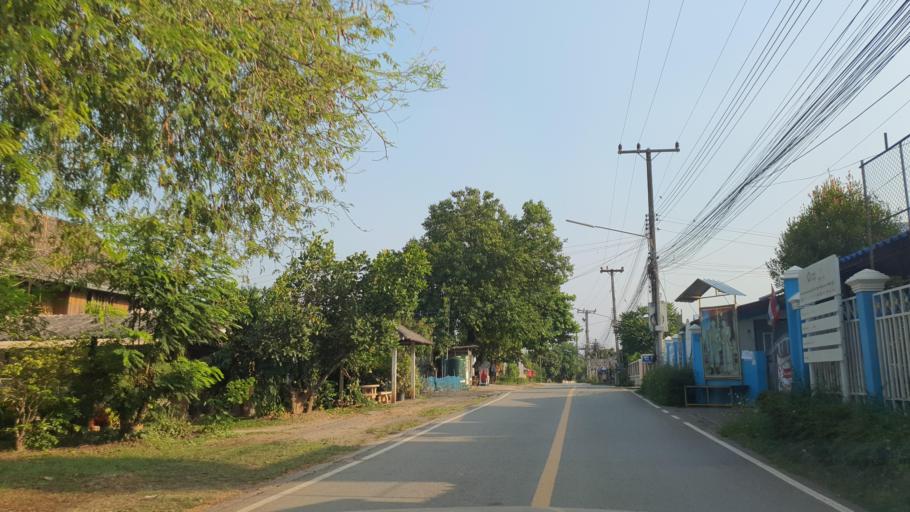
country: TH
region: Chiang Mai
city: Mae Wang
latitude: 18.6610
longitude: 98.8187
